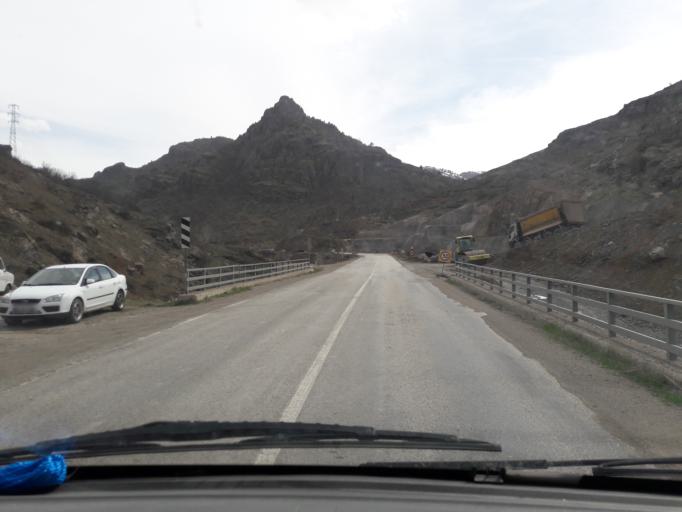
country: TR
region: Gumushane
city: Gumushkhane
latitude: 40.3018
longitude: 39.4741
